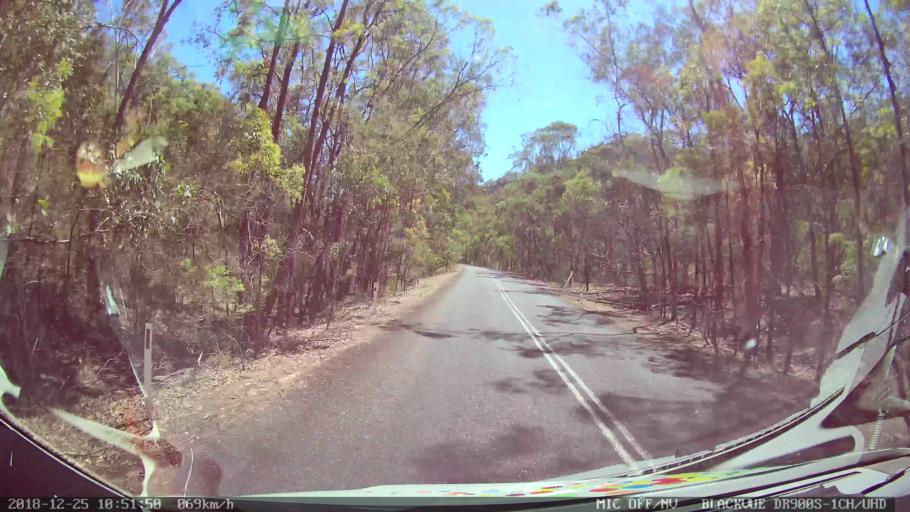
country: AU
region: New South Wales
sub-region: Upper Hunter Shire
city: Merriwa
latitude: -32.4338
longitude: 150.2711
